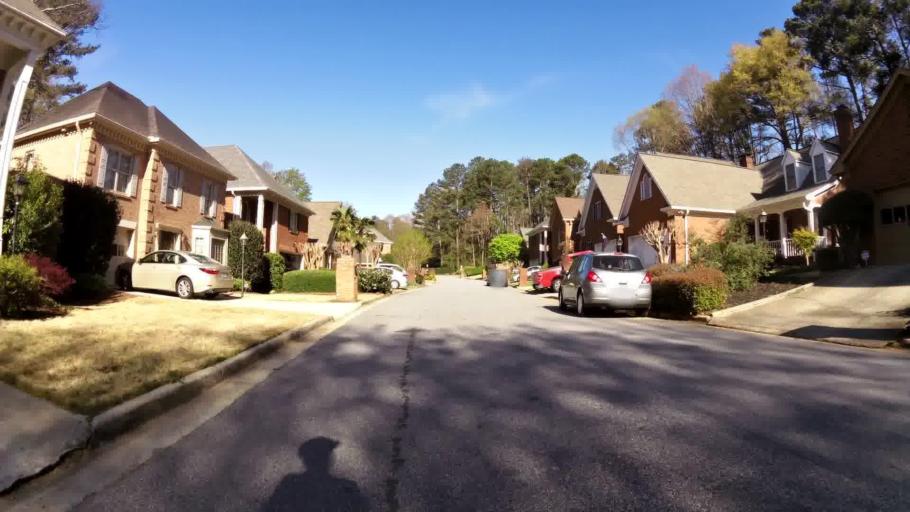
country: US
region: Georgia
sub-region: DeKalb County
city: Clarkston
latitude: 33.8336
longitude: -84.2684
